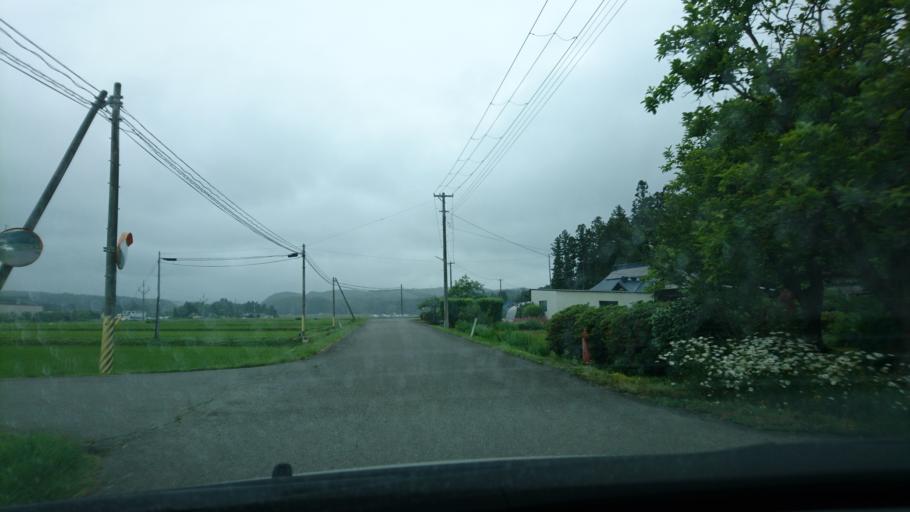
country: JP
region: Iwate
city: Ichinoseki
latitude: 38.9478
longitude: 141.0579
